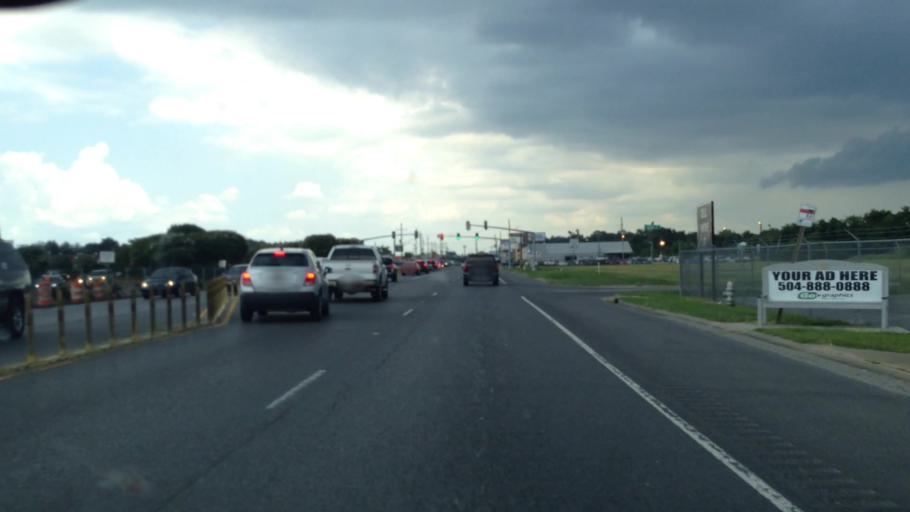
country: US
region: Louisiana
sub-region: Jefferson Parish
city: Kenner
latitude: 29.9814
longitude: -90.2530
